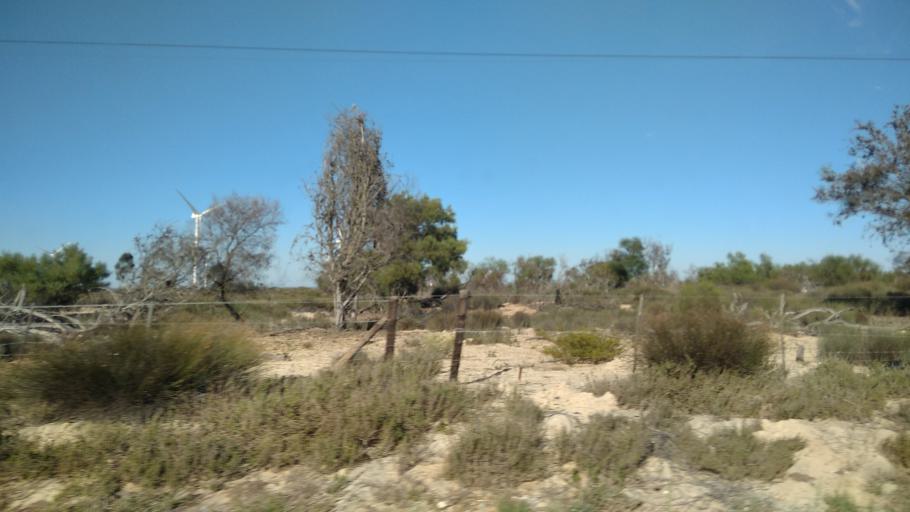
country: ZA
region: Western Cape
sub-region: West Coast District Municipality
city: Moorreesburg
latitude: -33.0755
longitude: 18.3802
